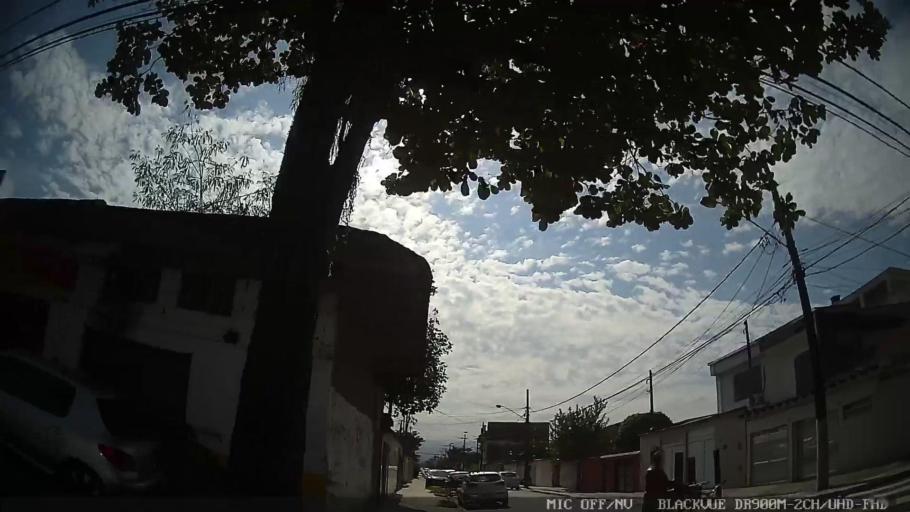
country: BR
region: Sao Paulo
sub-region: Santos
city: Santos
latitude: -23.9475
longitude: -46.2947
